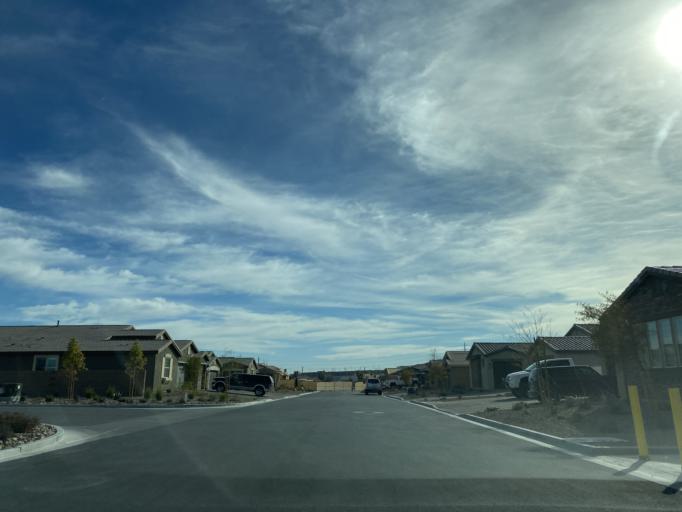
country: US
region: Nevada
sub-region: Clark County
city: Summerlin South
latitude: 36.2672
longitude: -115.3259
